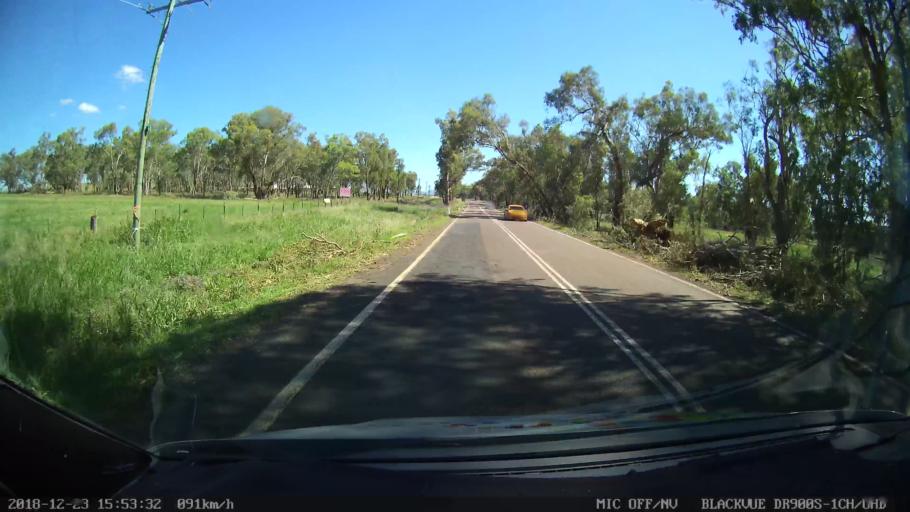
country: AU
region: New South Wales
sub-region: Tamworth Municipality
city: Phillip
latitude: -31.1344
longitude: 150.8803
